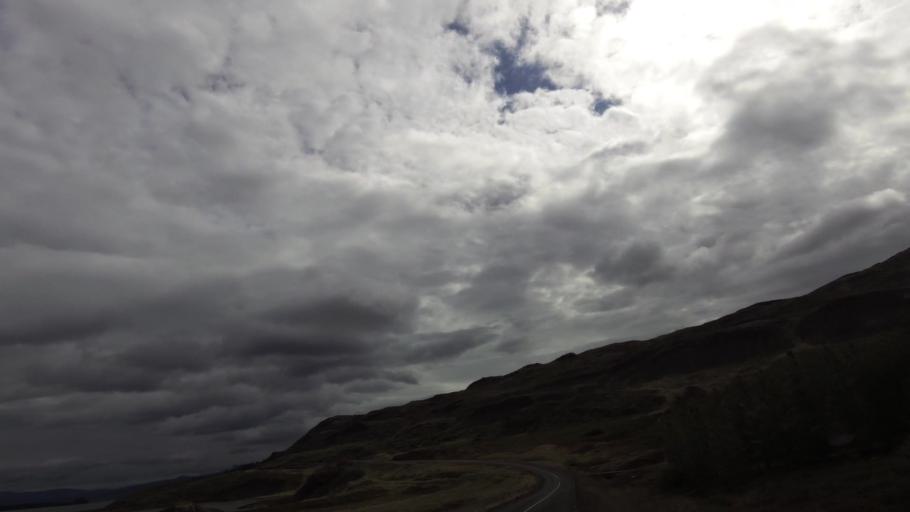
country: IS
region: West
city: Stykkisholmur
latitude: 65.5298
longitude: -22.1217
